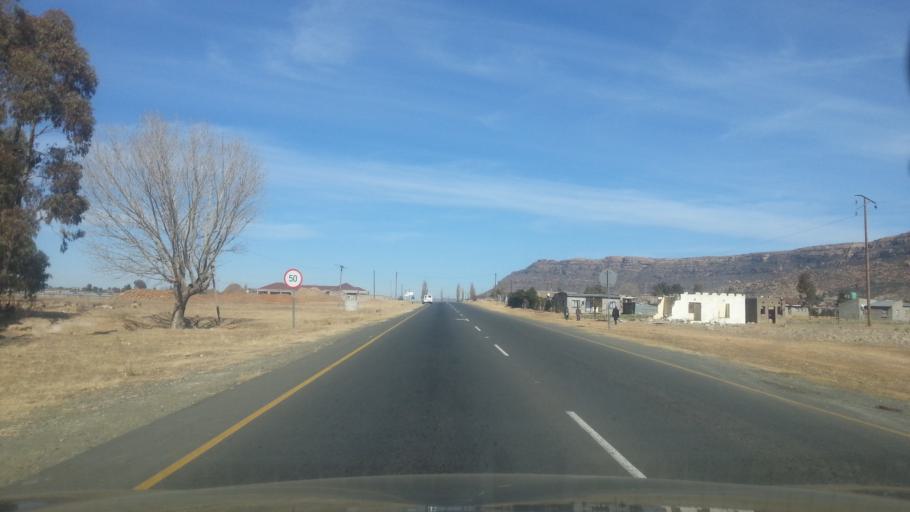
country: LS
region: Maseru
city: Maseru
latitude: -29.4784
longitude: 27.5290
